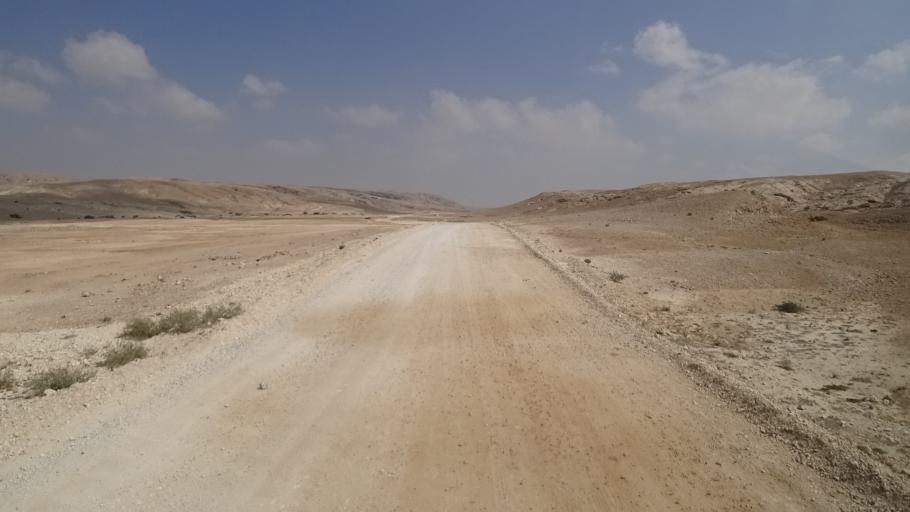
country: OM
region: Zufar
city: Salalah
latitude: 17.2376
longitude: 53.9005
